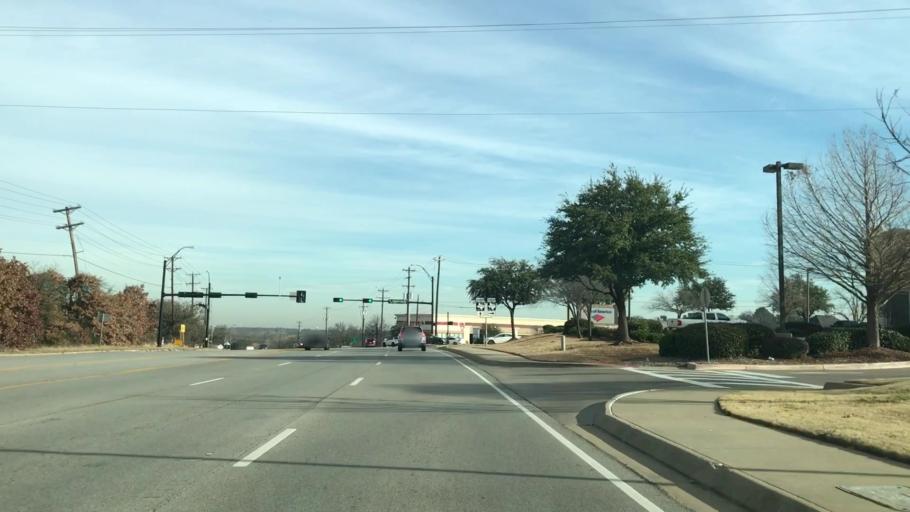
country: US
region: Texas
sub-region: Tarrant County
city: Colleyville
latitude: 32.9100
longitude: -97.1889
